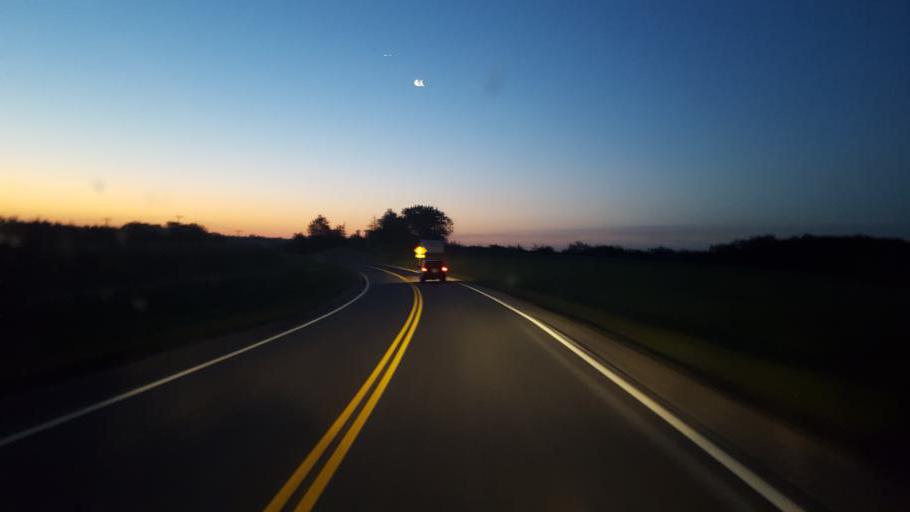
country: US
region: Missouri
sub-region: Mercer County
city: Princeton
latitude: 40.4096
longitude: -93.5374
